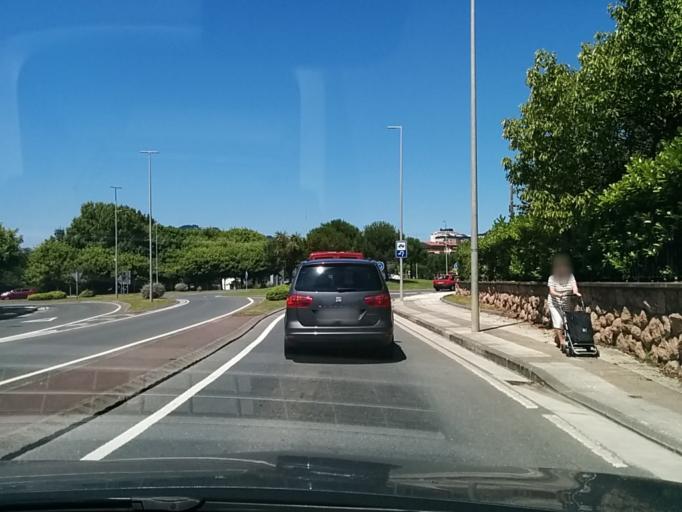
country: ES
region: Basque Country
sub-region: Provincia de Guipuzcoa
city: Zarautz
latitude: 43.2836
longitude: -2.1555
